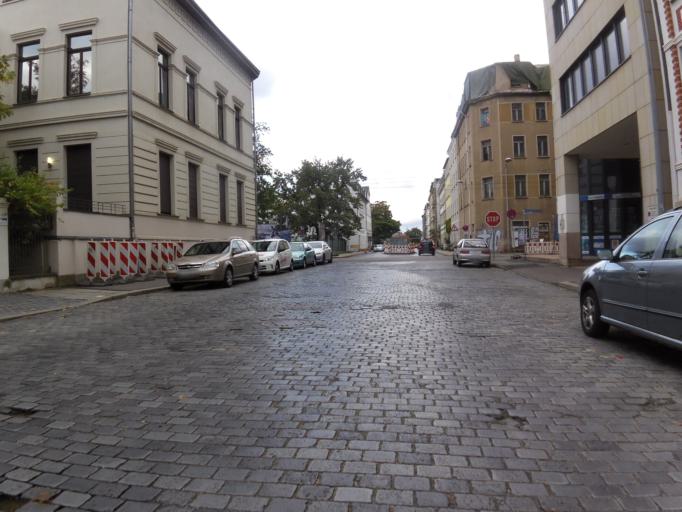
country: DE
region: Saxony
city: Leipzig
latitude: 51.3442
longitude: 12.3900
